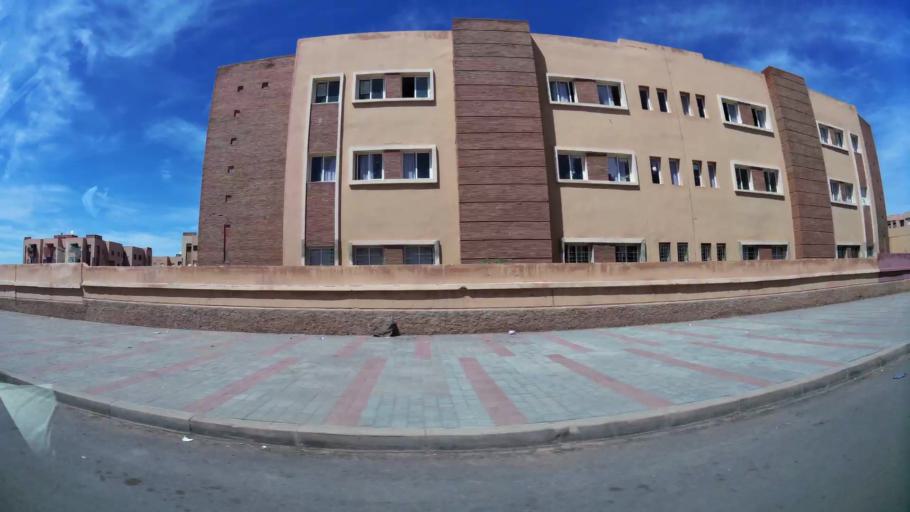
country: MA
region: Marrakech-Tensift-Al Haouz
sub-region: Marrakech
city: Marrakesh
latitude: 31.6395
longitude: -8.0806
